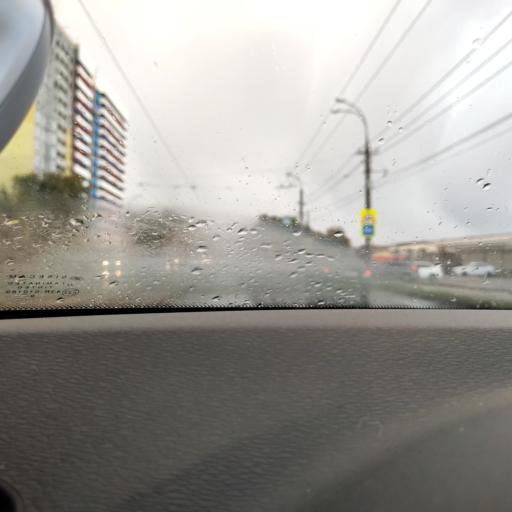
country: RU
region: Samara
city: Smyshlyayevka
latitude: 53.2028
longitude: 50.2823
